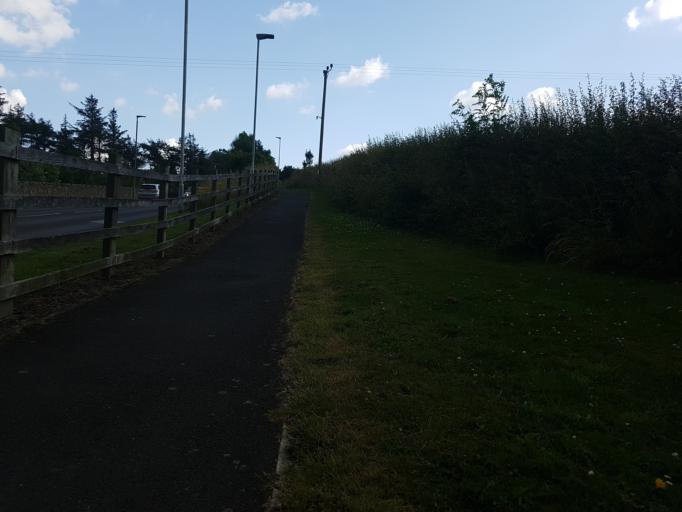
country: GB
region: England
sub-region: Northumberland
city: Alnmouth
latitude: 55.3965
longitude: -1.6342
